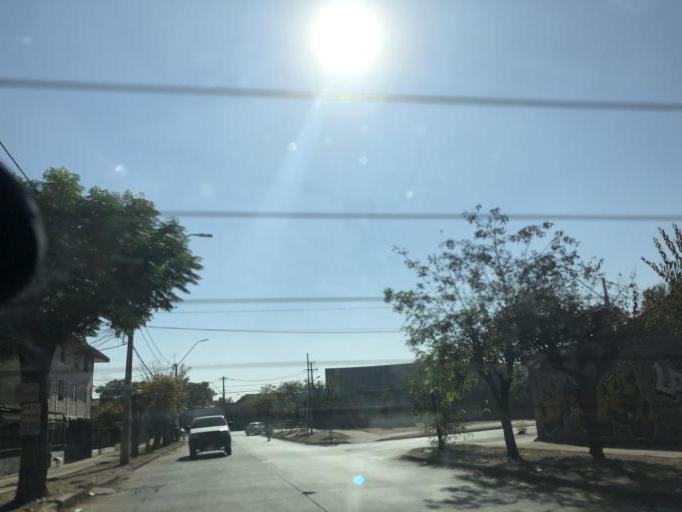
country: CL
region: Santiago Metropolitan
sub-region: Provincia de Cordillera
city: Puente Alto
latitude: -33.6087
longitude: -70.5842
